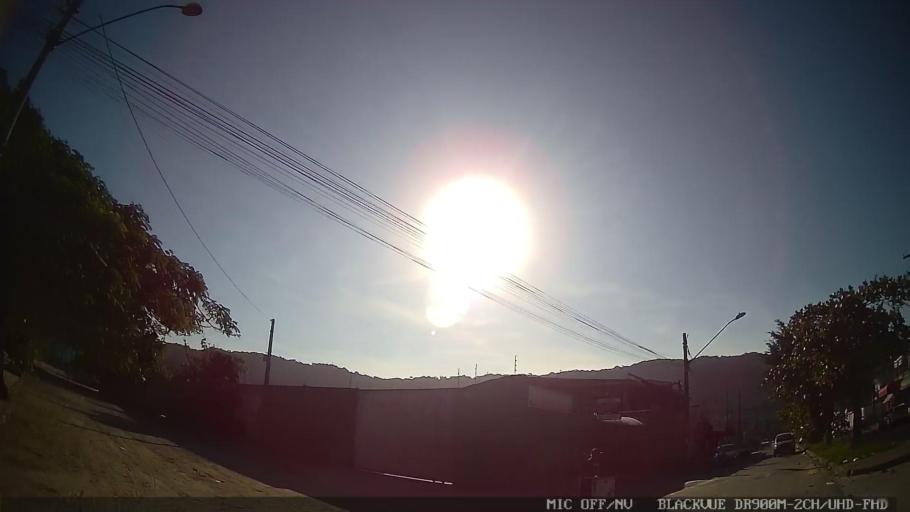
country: BR
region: Sao Paulo
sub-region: Guaruja
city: Guaruja
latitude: -23.9746
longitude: -46.2232
